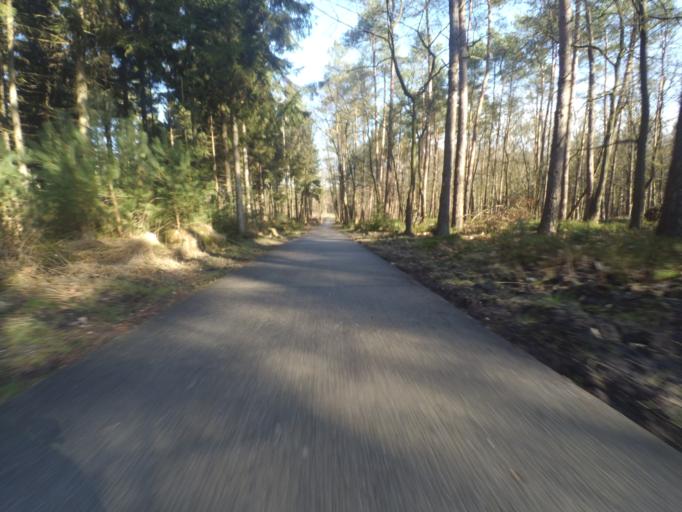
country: NL
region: Gelderland
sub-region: Gemeente Apeldoorn
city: Beekbergen
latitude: 52.1828
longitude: 5.8828
